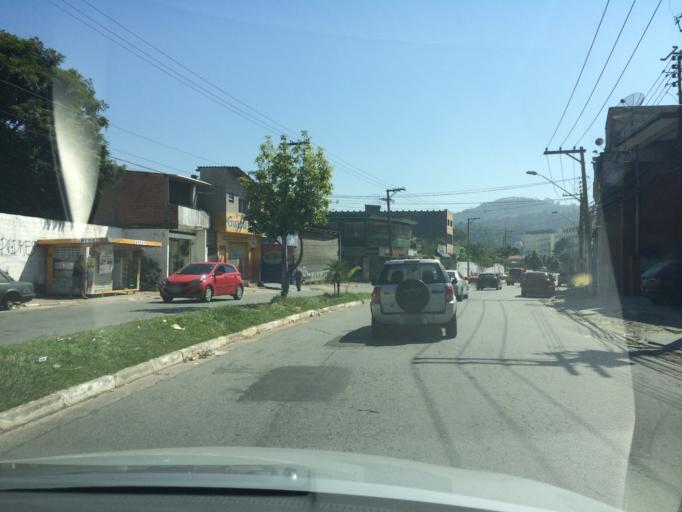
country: BR
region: Sao Paulo
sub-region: Guarulhos
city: Guarulhos
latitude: -23.4334
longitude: -46.5375
